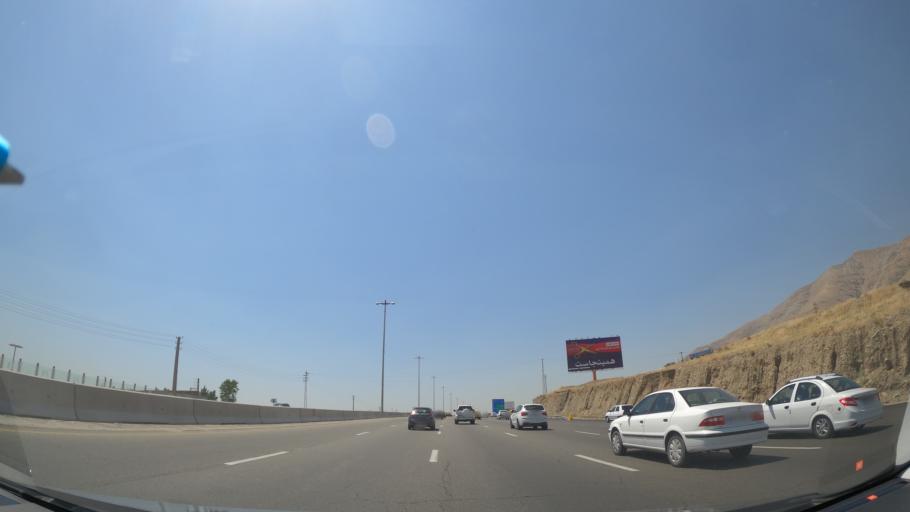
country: IR
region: Tehran
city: Shahr-e Qods
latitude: 35.7472
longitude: 51.0864
